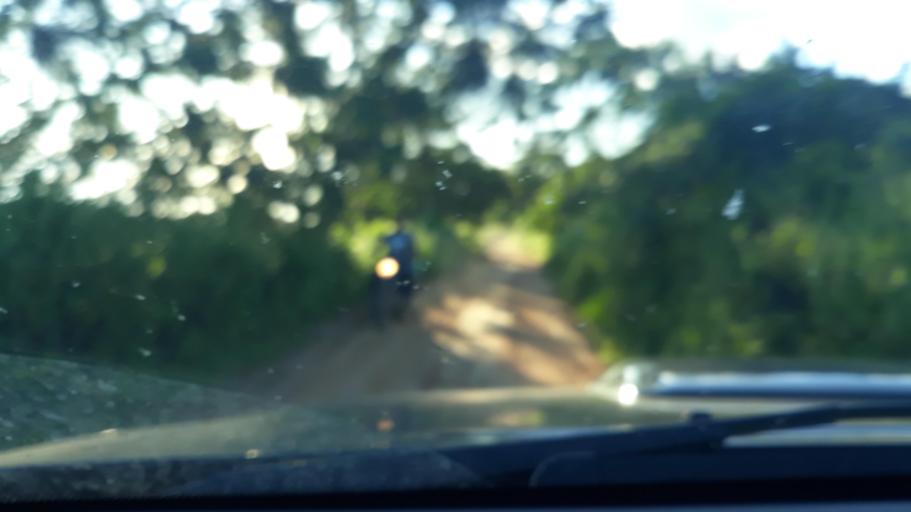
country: BR
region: Bahia
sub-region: Riacho De Santana
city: Riacho de Santana
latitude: -13.8459
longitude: -42.7587
